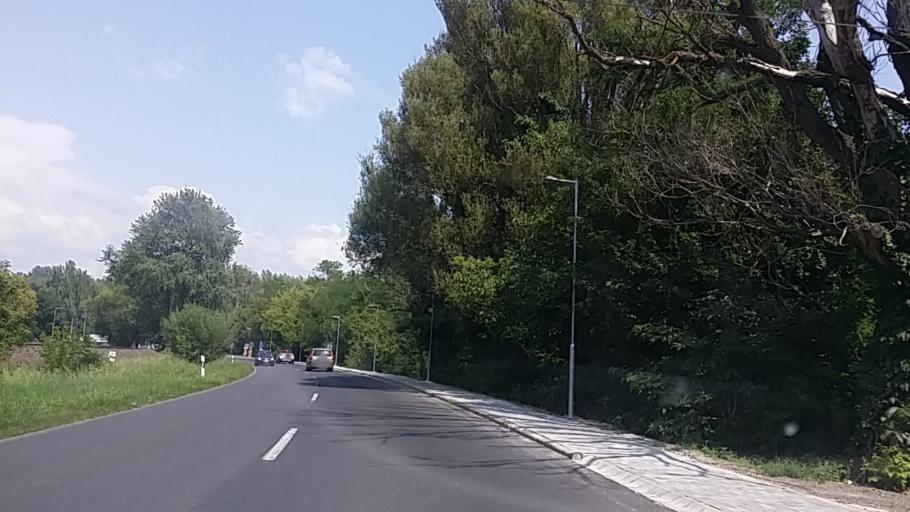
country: HU
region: Veszprem
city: Badacsonytomaj
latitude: 46.7846
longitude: 17.5021
